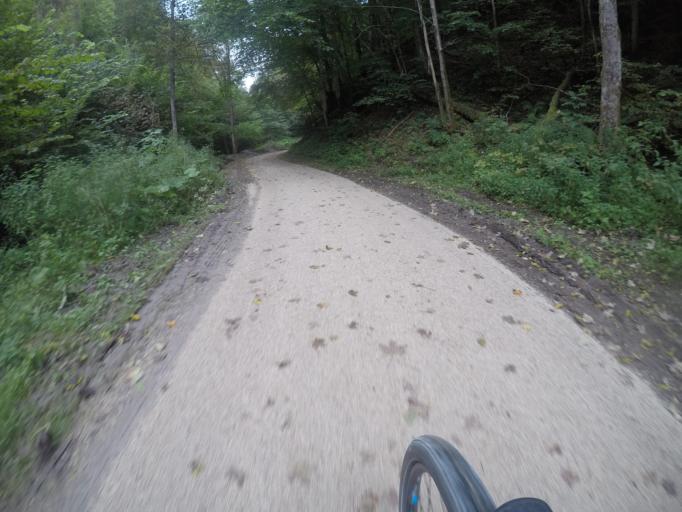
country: DE
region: Baden-Wuerttemberg
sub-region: Tuebingen Region
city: Munsingen
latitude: 48.4423
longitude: 9.4659
